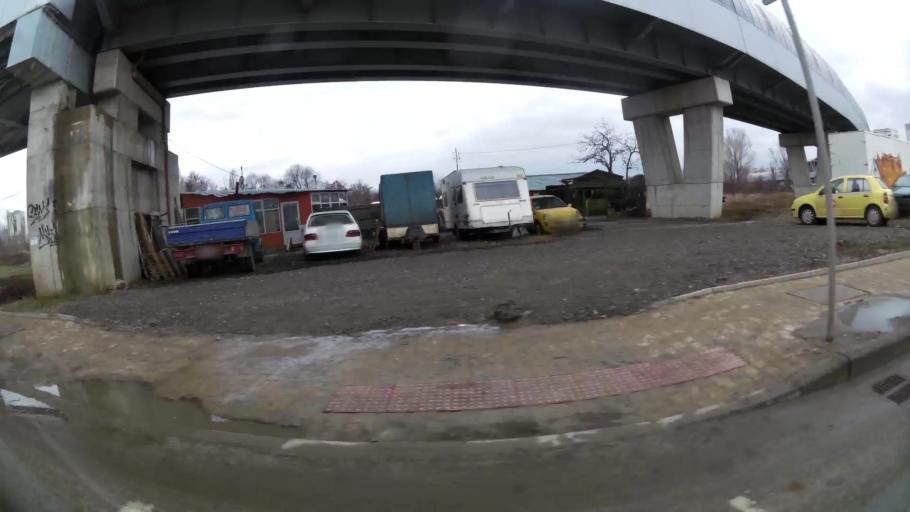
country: BG
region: Sofia-Capital
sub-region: Stolichna Obshtina
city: Sofia
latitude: 42.7422
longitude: 23.2853
